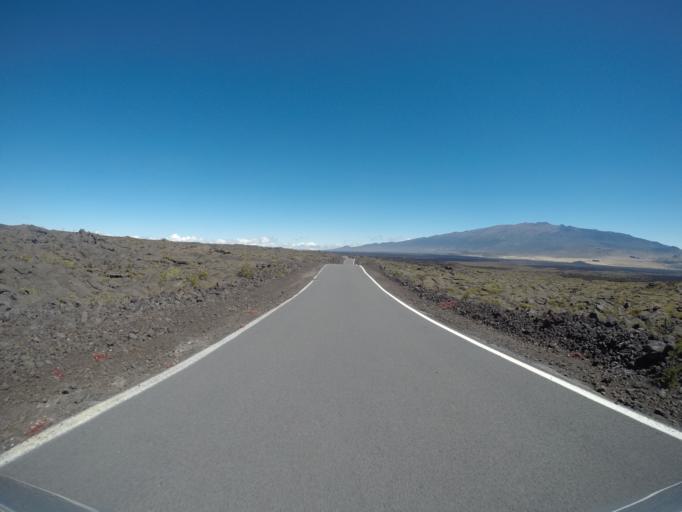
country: US
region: Hawaii
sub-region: Hawaii County
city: Volcano
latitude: 19.6252
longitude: -155.4761
